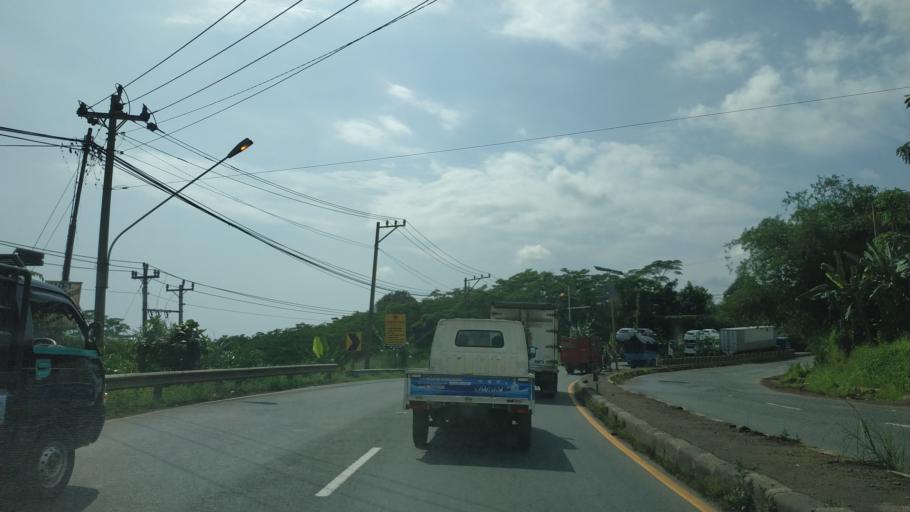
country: ID
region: Central Java
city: Pekalongan
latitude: -6.9244
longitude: 109.7611
